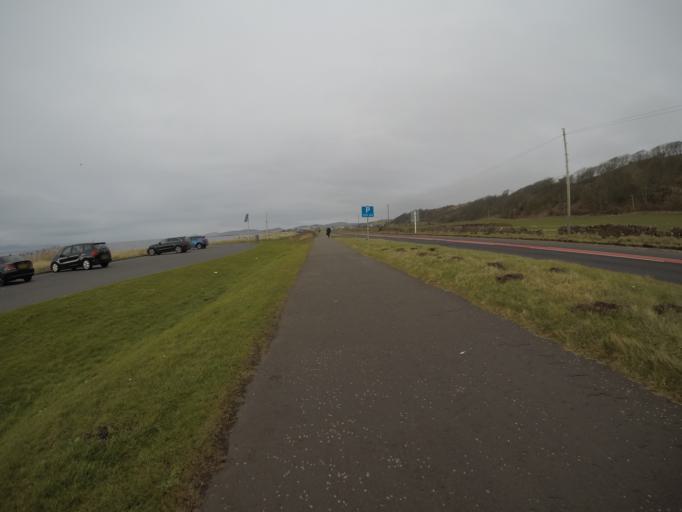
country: GB
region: Scotland
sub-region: North Ayrshire
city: West Kilbride
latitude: 55.6694
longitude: -4.8448
